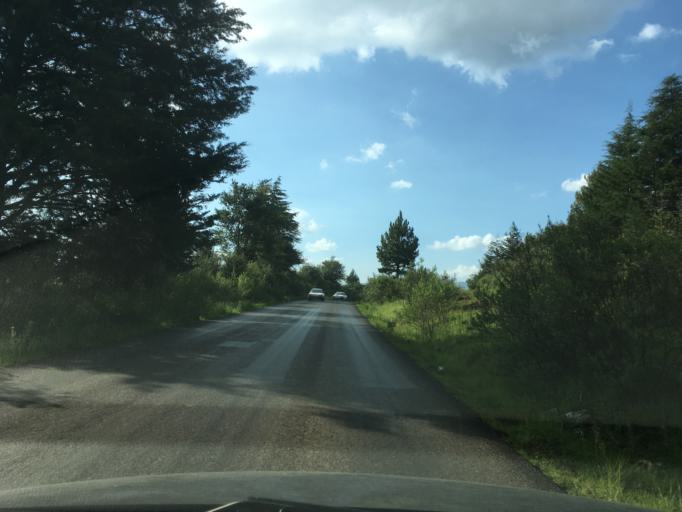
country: MX
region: Michoacan
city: Nahuatzen
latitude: 19.6378
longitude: -101.9260
